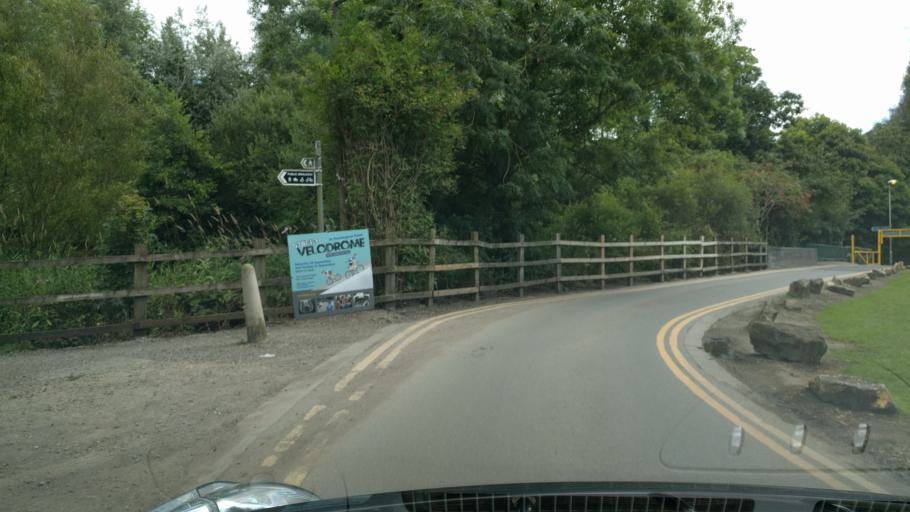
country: GB
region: England
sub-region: Borough of Wigan
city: Leigh
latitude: 53.4858
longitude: -2.5350
